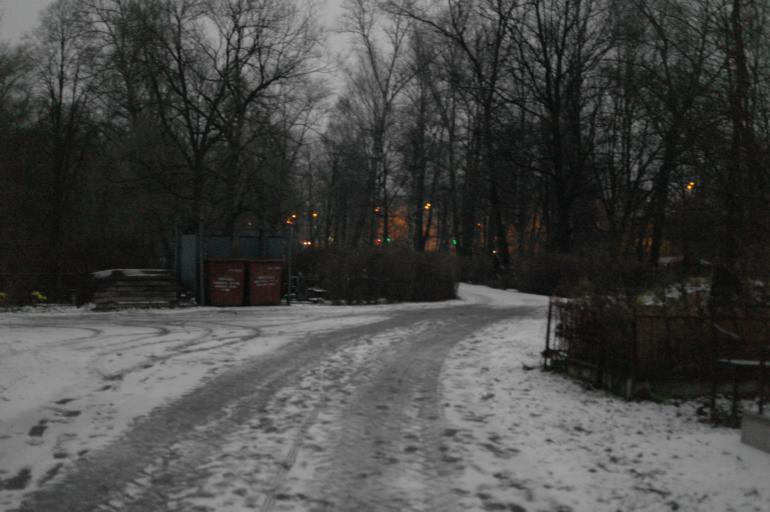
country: RU
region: St.-Petersburg
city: Centralniy
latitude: 59.8984
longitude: 30.3556
